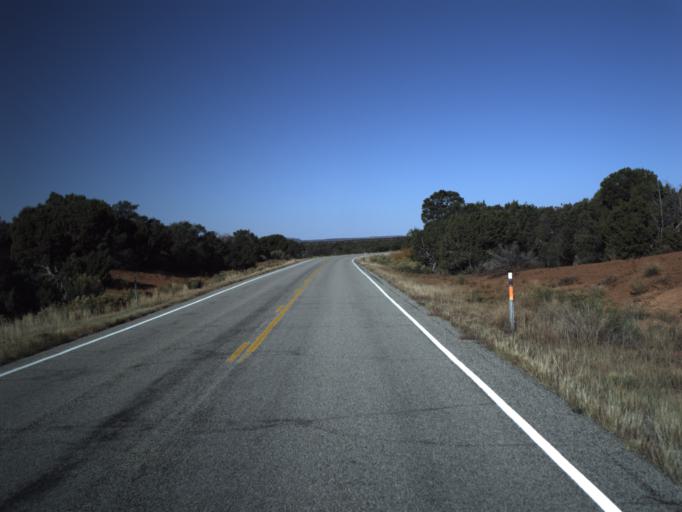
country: US
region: Utah
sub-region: San Juan County
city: Blanding
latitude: 37.5660
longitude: -109.8633
